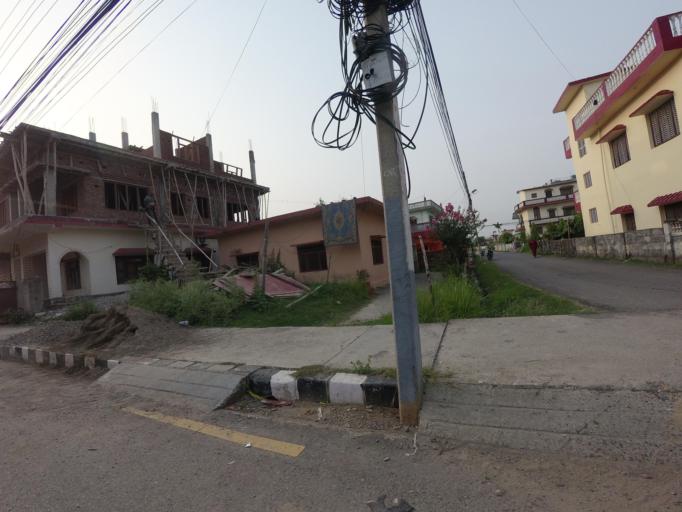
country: NP
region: Western Region
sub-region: Lumbini Zone
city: Bhairahawa
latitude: 27.5141
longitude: 83.4574
